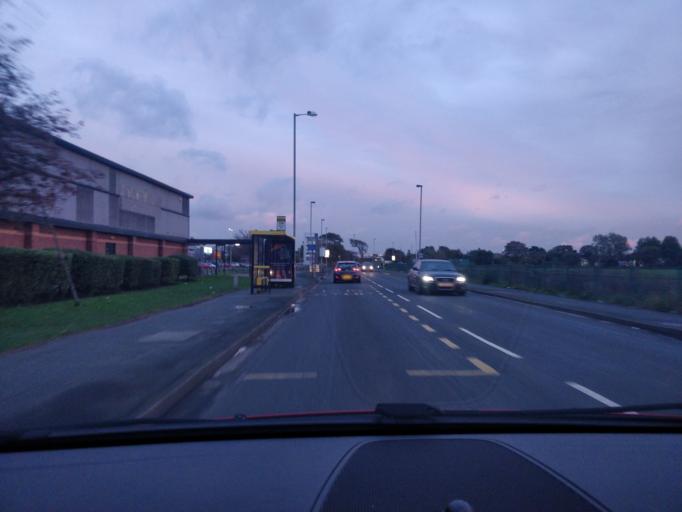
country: GB
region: England
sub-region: Sefton
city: Southport
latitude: 53.6367
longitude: -2.9714
